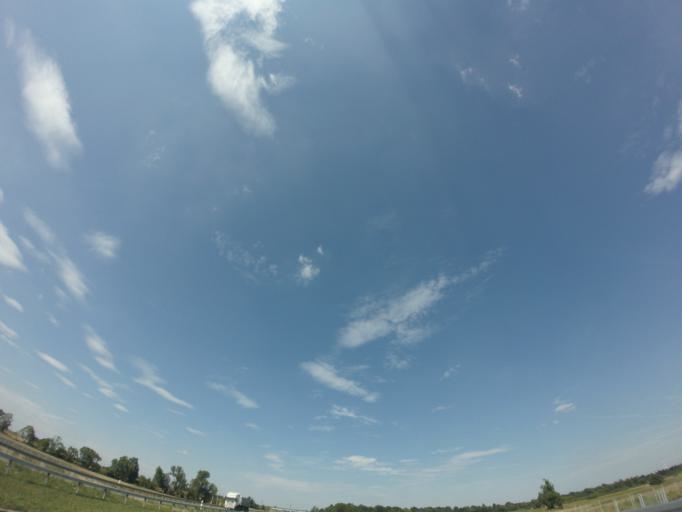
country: PL
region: Lower Silesian Voivodeship
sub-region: Legnica
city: Legnica
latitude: 51.2255
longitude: 16.1397
